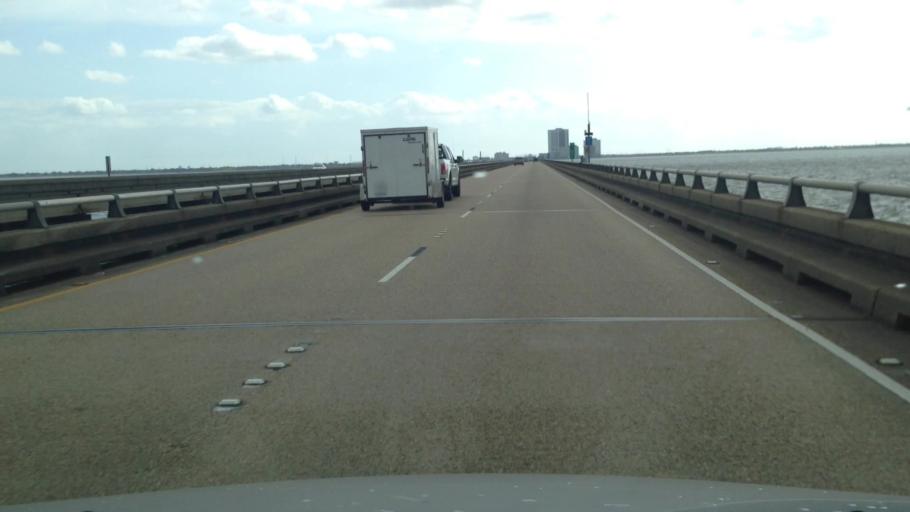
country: US
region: Louisiana
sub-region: Jefferson Parish
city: Metairie
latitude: 30.0526
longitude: -90.1487
